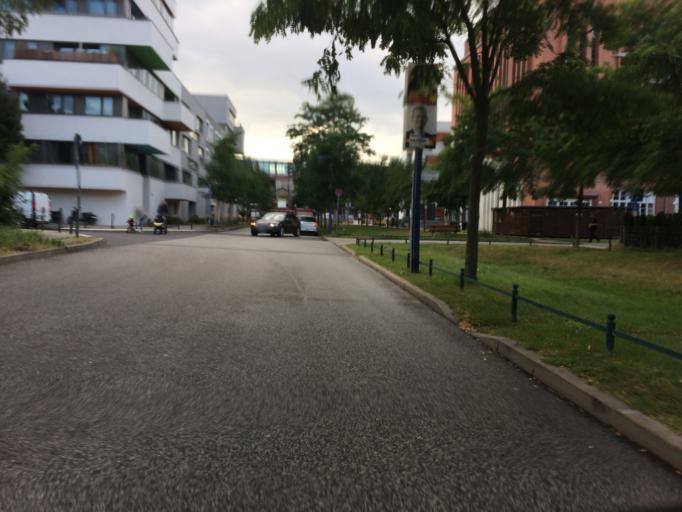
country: DE
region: Berlin
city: Treptow Bezirk
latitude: 52.4969
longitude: 13.4705
